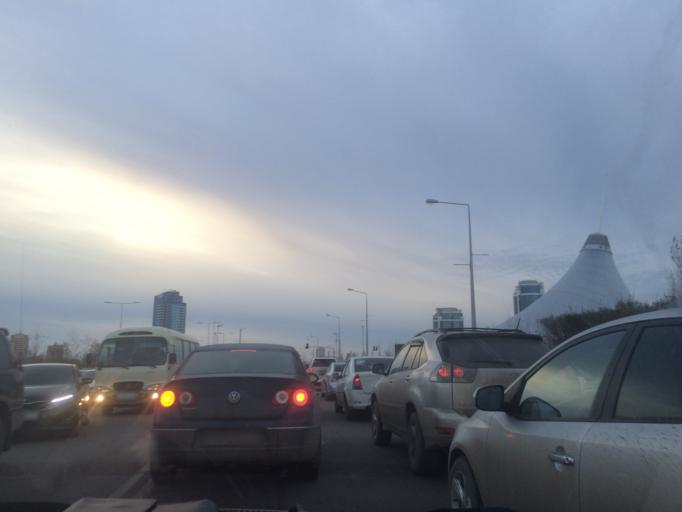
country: KZ
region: Astana Qalasy
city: Astana
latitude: 51.1358
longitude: 71.4081
